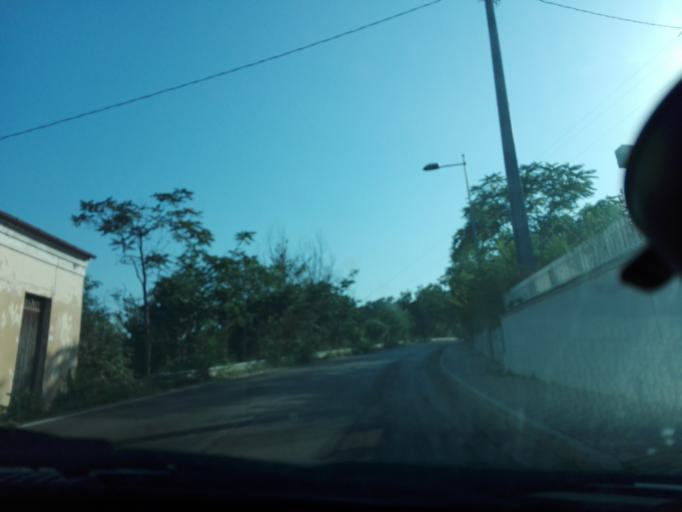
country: IT
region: Abruzzo
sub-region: Provincia di Pescara
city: Cappelle sul Tavo
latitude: 42.4710
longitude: 14.1082
